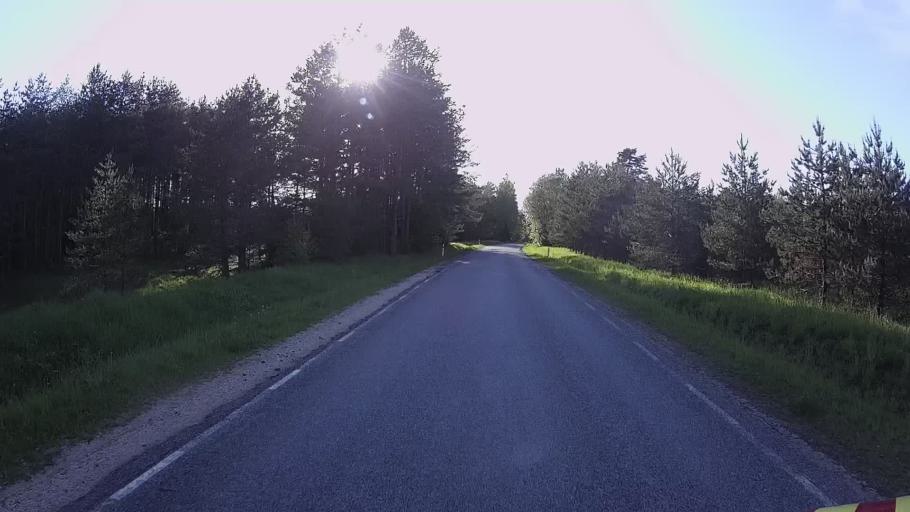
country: EE
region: Laeaene-Virumaa
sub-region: Vinni vald
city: Vinni
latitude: 59.2928
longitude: 26.5882
